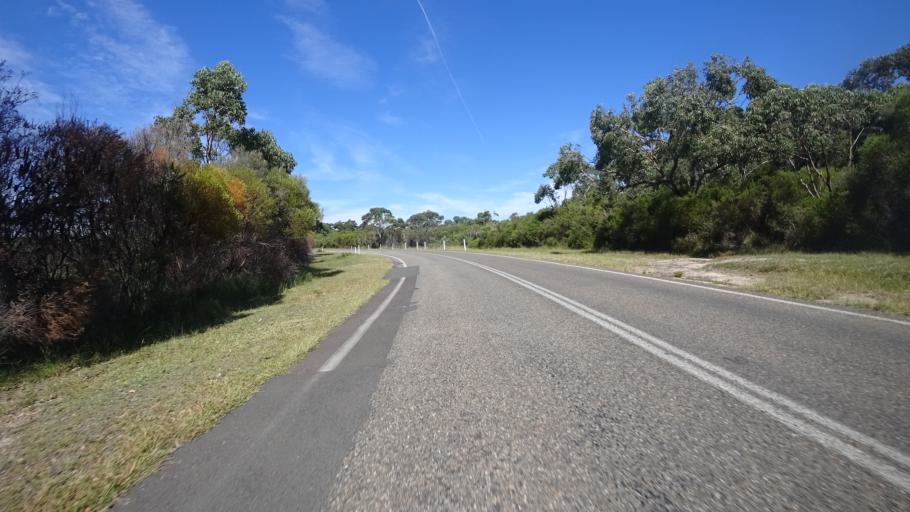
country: AU
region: New South Wales
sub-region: Shoalhaven Shire
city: Falls Creek
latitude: -35.1425
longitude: 150.7046
